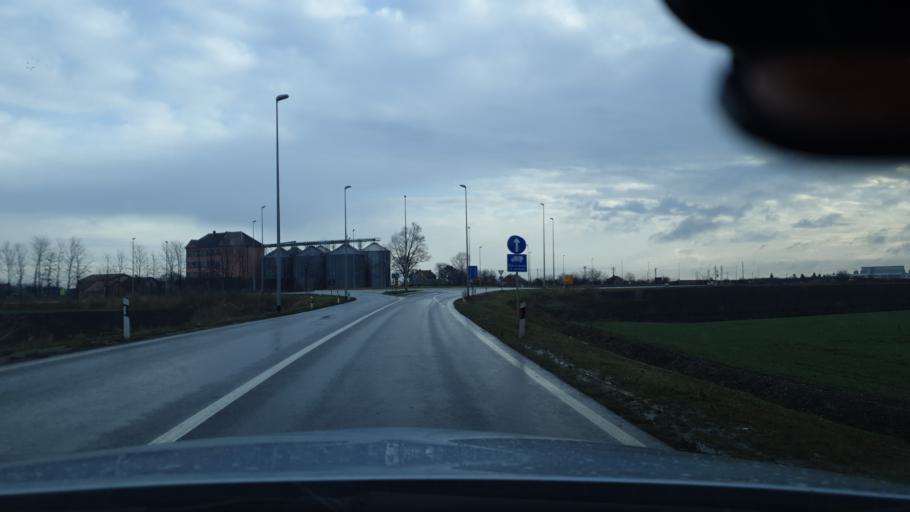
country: RS
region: Autonomna Pokrajina Vojvodina
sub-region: Juznobanatski Okrug
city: Kovin
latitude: 44.8101
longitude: 20.8864
